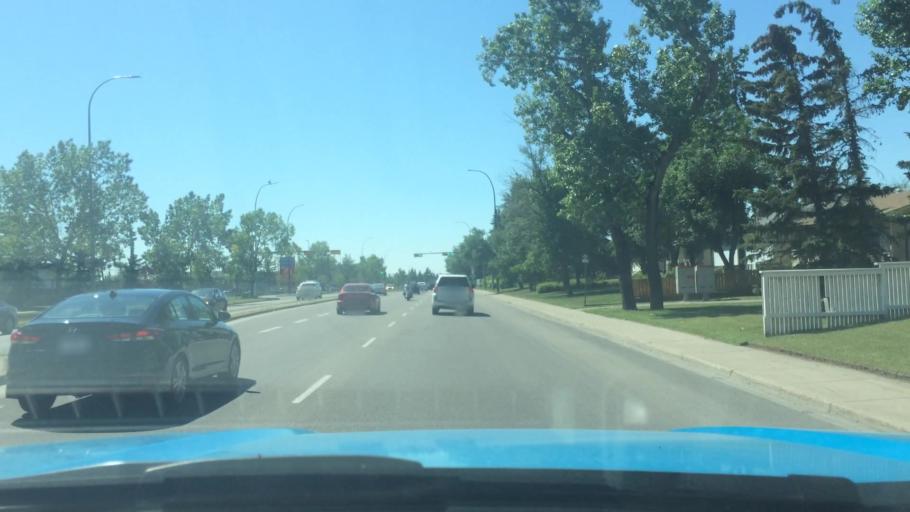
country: CA
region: Alberta
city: Calgary
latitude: 51.0562
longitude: -113.9571
